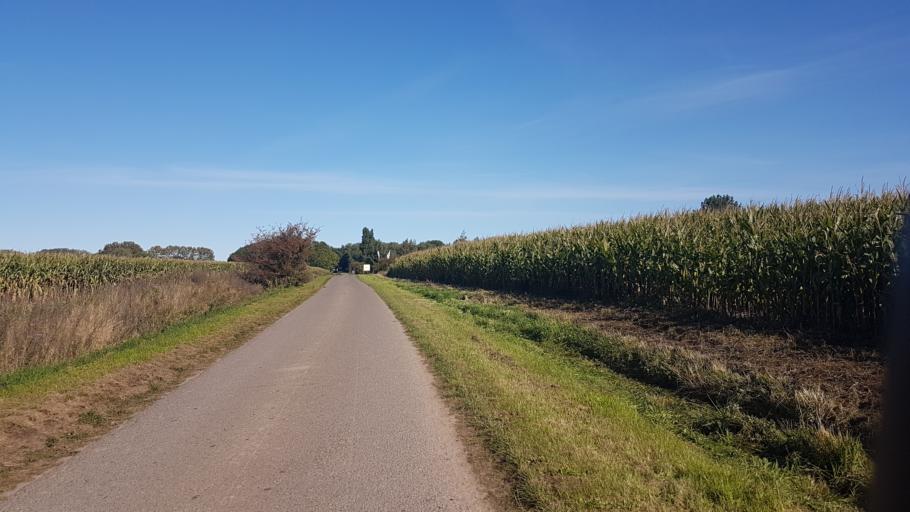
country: DE
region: Mecklenburg-Vorpommern
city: Sagard
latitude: 54.5147
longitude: 13.5302
